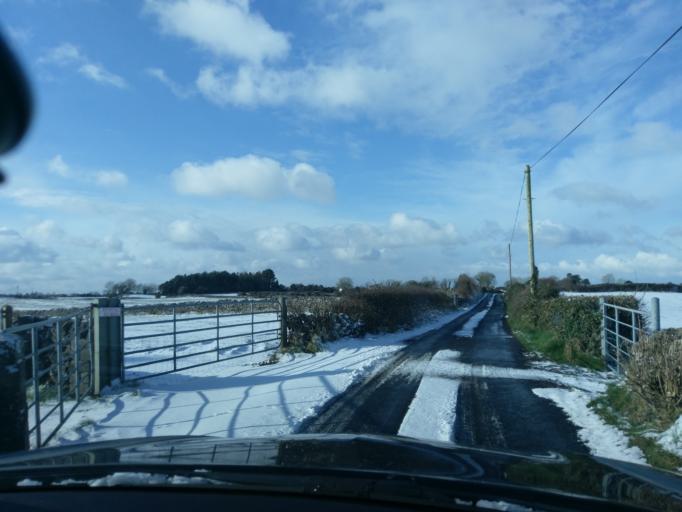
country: IE
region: Connaught
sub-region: County Galway
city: Athenry
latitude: 53.2023
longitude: -8.8093
